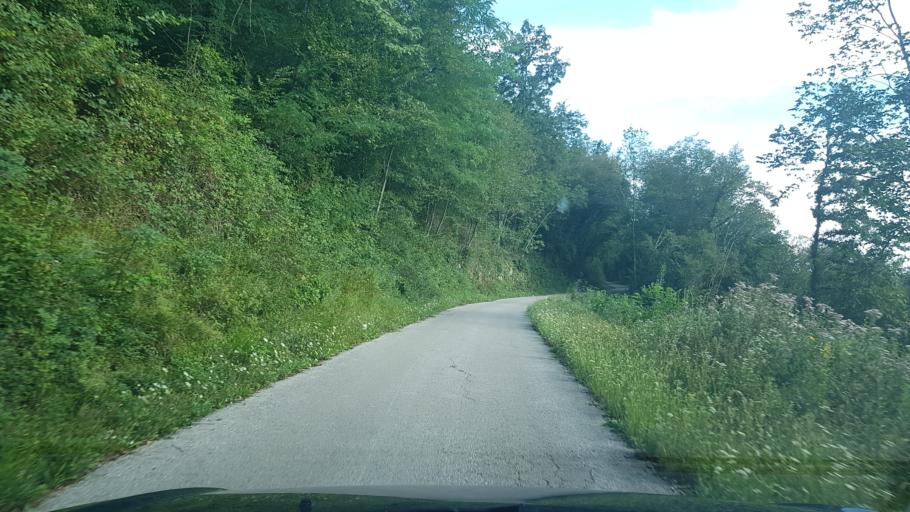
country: SI
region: Kanal
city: Deskle
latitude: 46.0281
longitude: 13.6095
